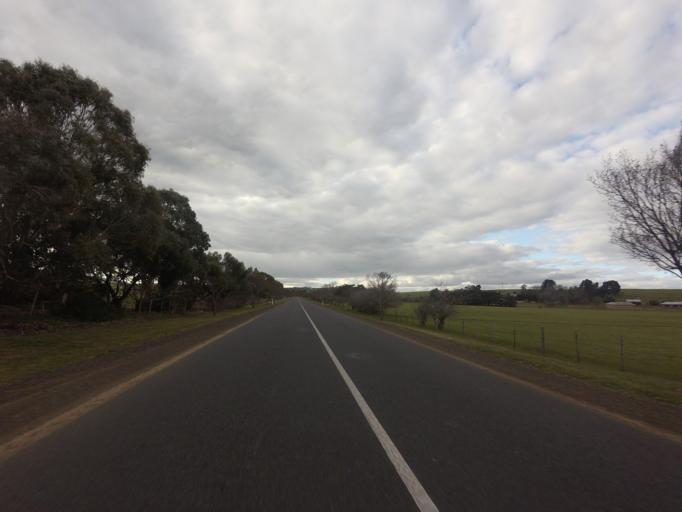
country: AU
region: Tasmania
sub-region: Northern Midlands
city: Evandale
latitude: -42.0209
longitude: 147.4922
